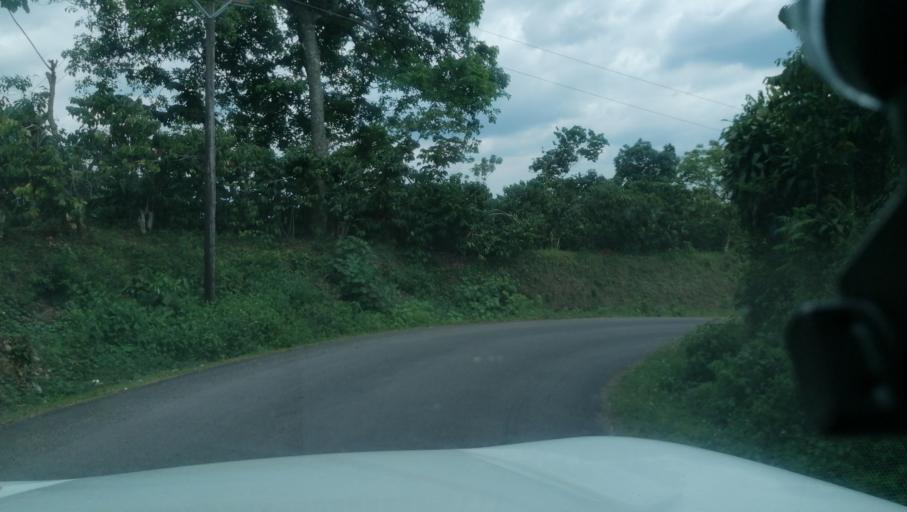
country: MX
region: Chiapas
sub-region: Cacahoatan
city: Benito Juarez
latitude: 15.0505
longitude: -92.1522
